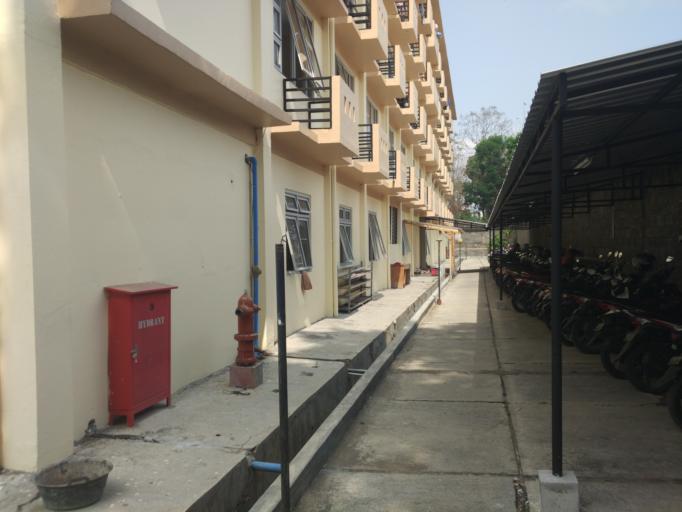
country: ID
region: Daerah Istimewa Yogyakarta
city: Sleman
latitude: -7.6866
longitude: 110.4144
